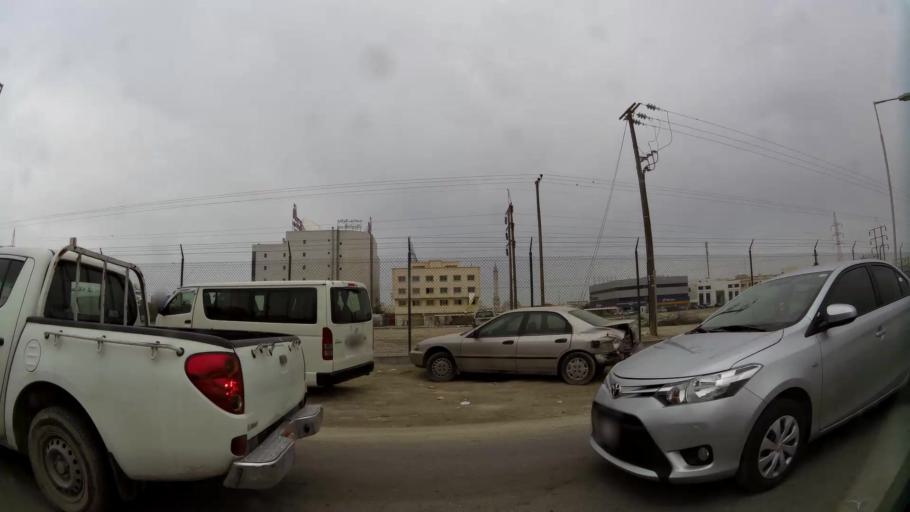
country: BH
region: Northern
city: Madinat `Isa
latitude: 26.1845
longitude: 50.5347
